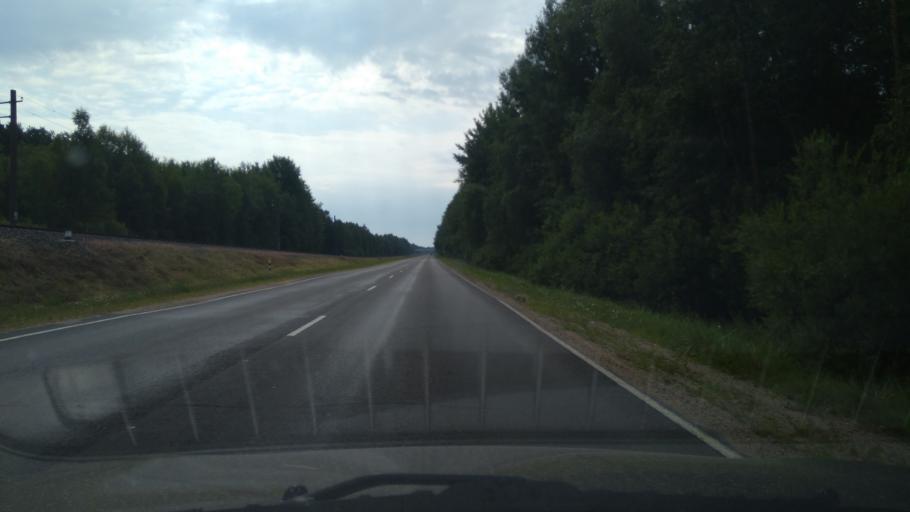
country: BY
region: Brest
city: Nyakhachava
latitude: 52.5847
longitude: 25.0994
